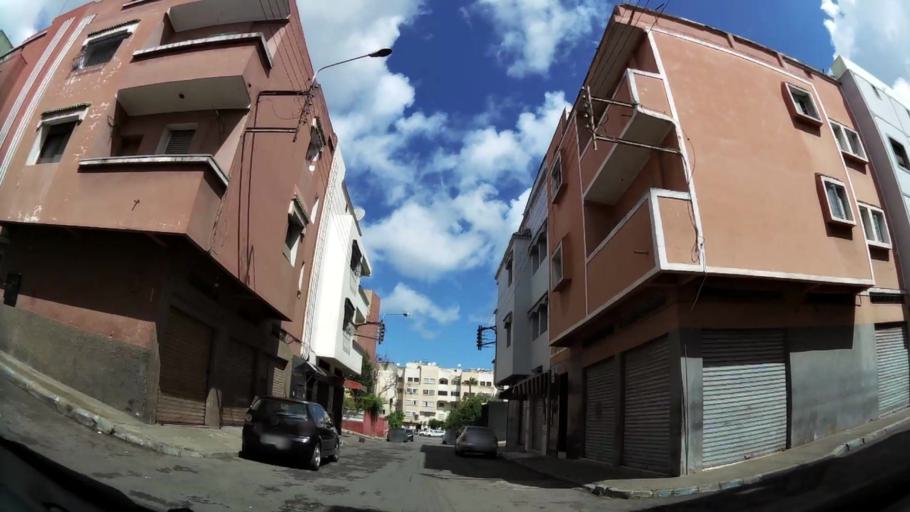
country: MA
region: Grand Casablanca
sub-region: Casablanca
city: Casablanca
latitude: 33.5418
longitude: -7.5874
